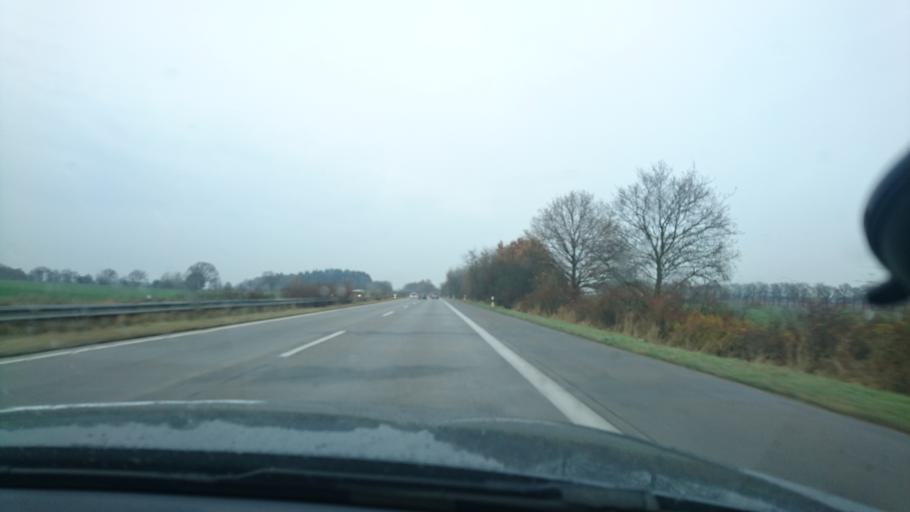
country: DE
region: Schleswig-Holstein
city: Ratekau
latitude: 53.9824
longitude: 10.7333
